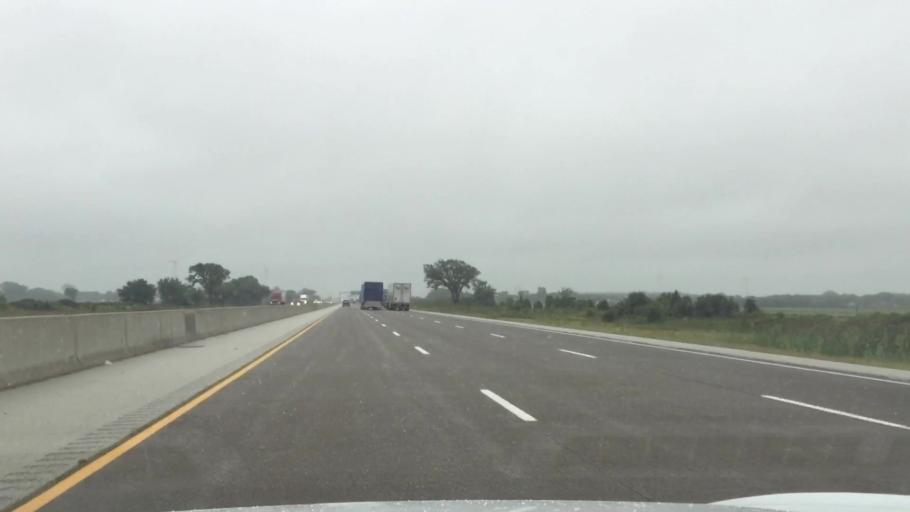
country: US
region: Michigan
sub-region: Wayne County
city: Grosse Pointe
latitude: 42.2370
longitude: -82.7326
